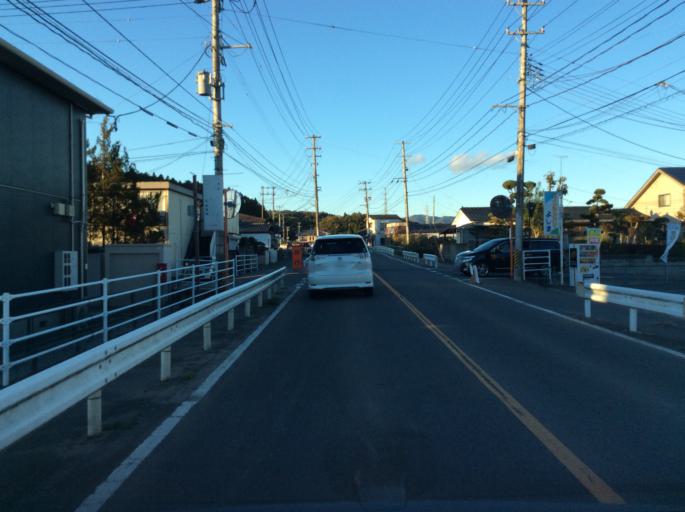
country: JP
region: Fukushima
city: Iwaki
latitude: 37.0615
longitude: 140.8707
